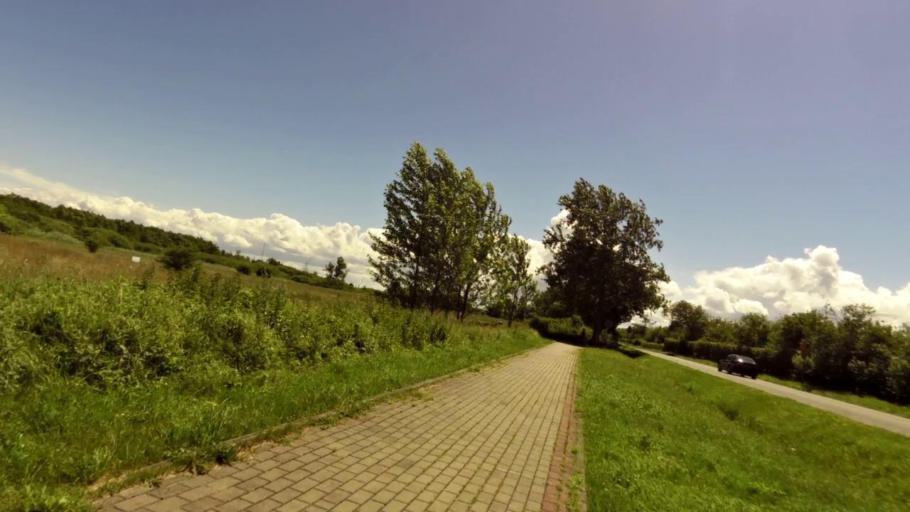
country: PL
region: West Pomeranian Voivodeship
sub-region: Koszalin
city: Koszalin
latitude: 54.3024
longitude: 16.2015
